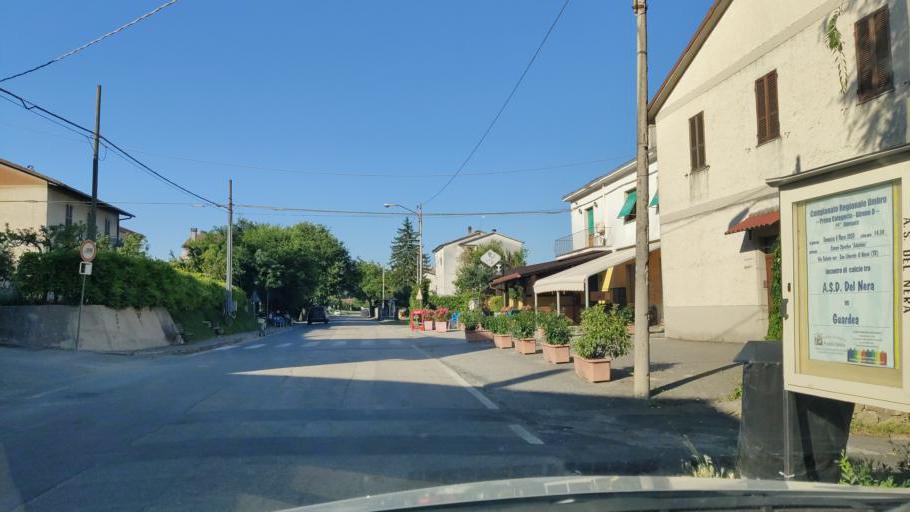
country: IT
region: Latium
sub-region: Provincia di Viterbo
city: Orte Scalo
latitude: 42.4784
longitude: 12.4374
